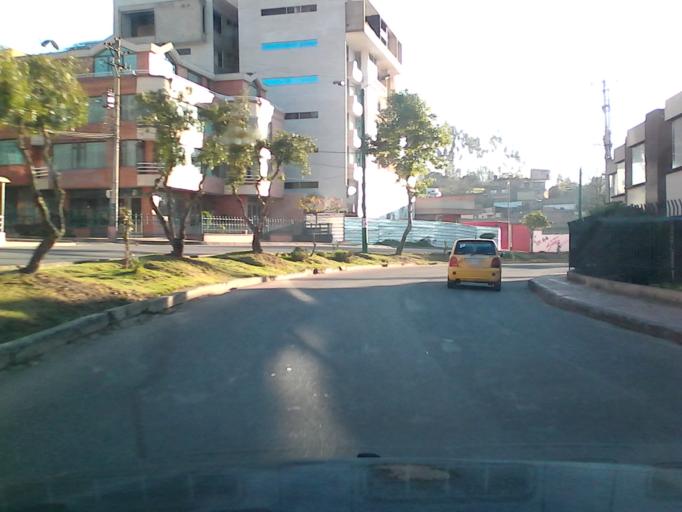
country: CO
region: Boyaca
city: Duitama
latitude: 5.8357
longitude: -73.0326
